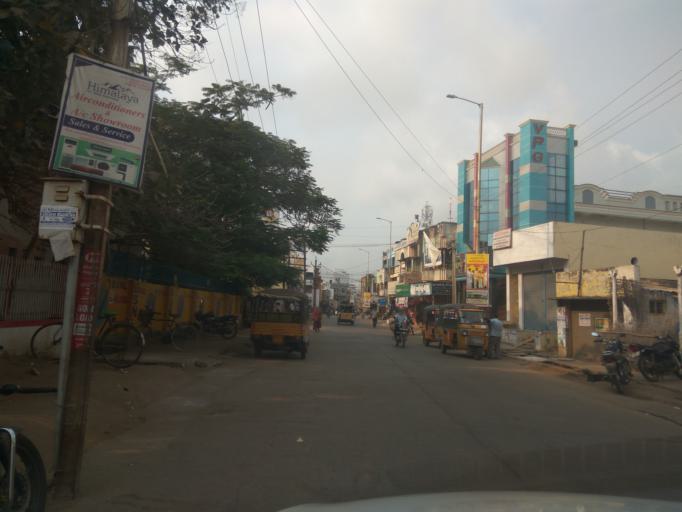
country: IN
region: Andhra Pradesh
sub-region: Prakasam
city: Kandukur
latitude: 15.2163
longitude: 79.9039
